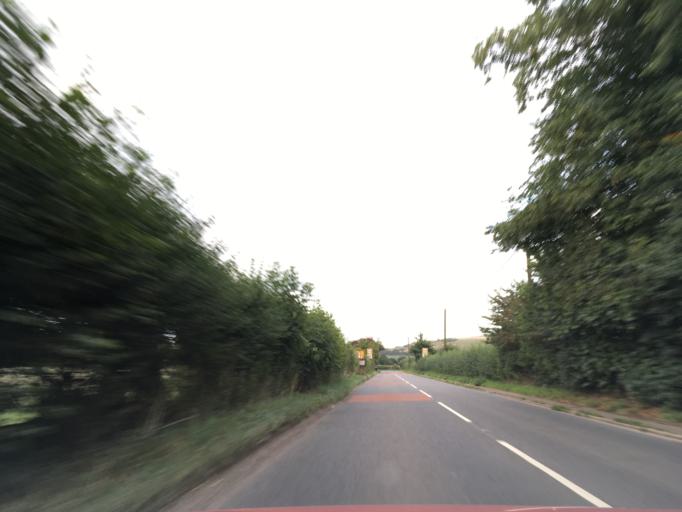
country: GB
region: England
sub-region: Wiltshire
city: Devizes
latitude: 51.3725
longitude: -2.0345
